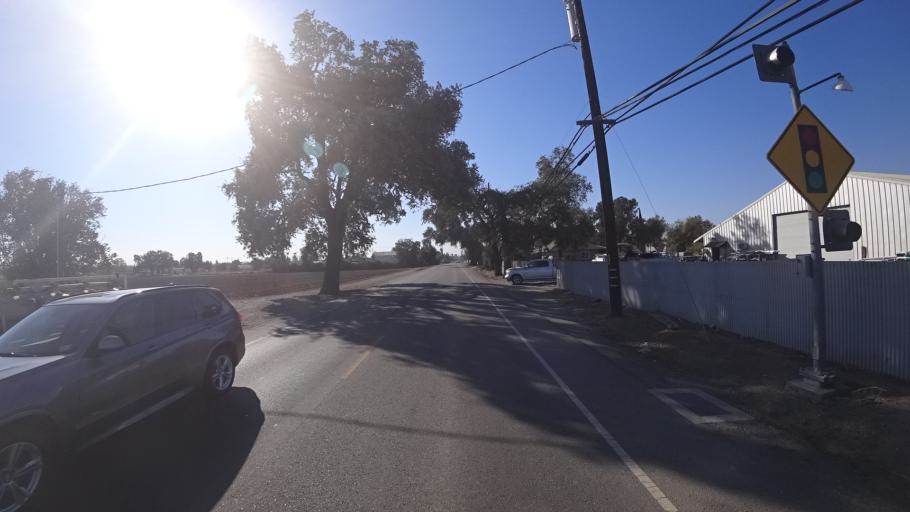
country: US
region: California
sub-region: Yolo County
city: Woodland
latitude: 38.6945
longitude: -121.7839
